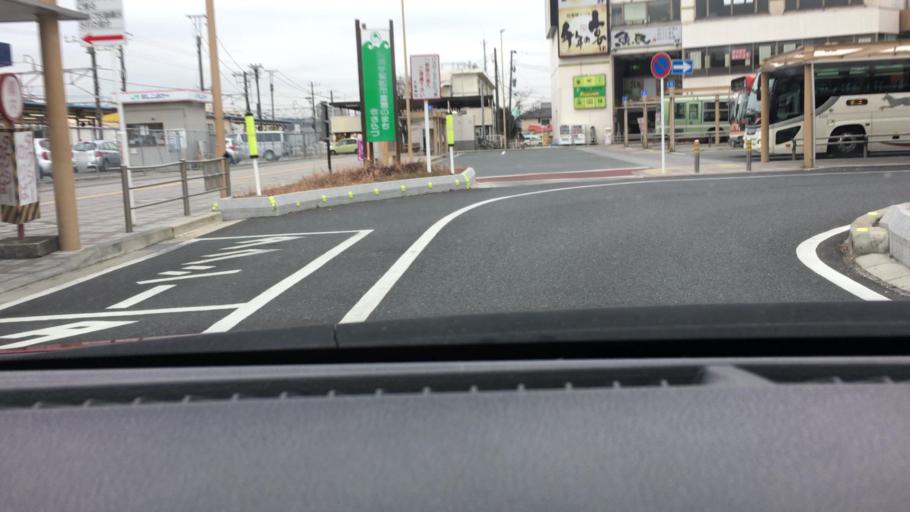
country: JP
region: Chiba
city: Kisarazu
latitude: 35.3815
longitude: 139.9256
